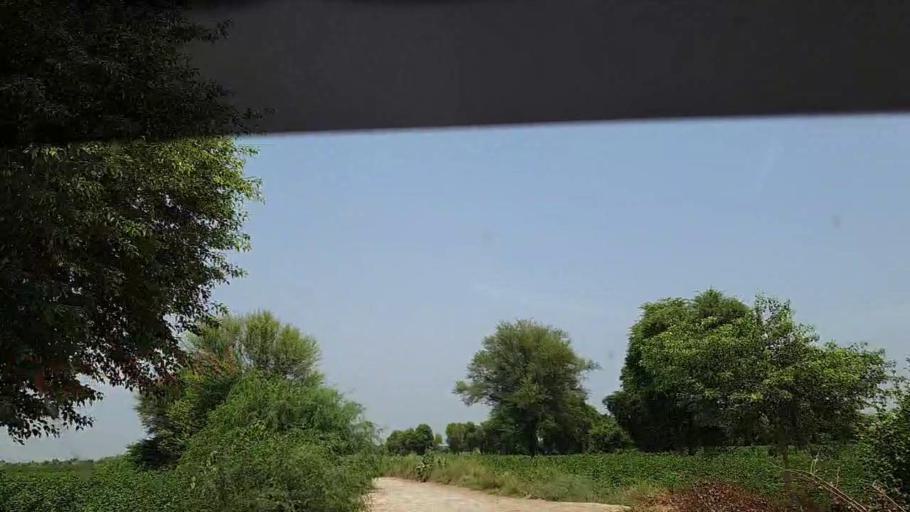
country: PK
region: Sindh
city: Adilpur
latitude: 27.8834
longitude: 69.2591
